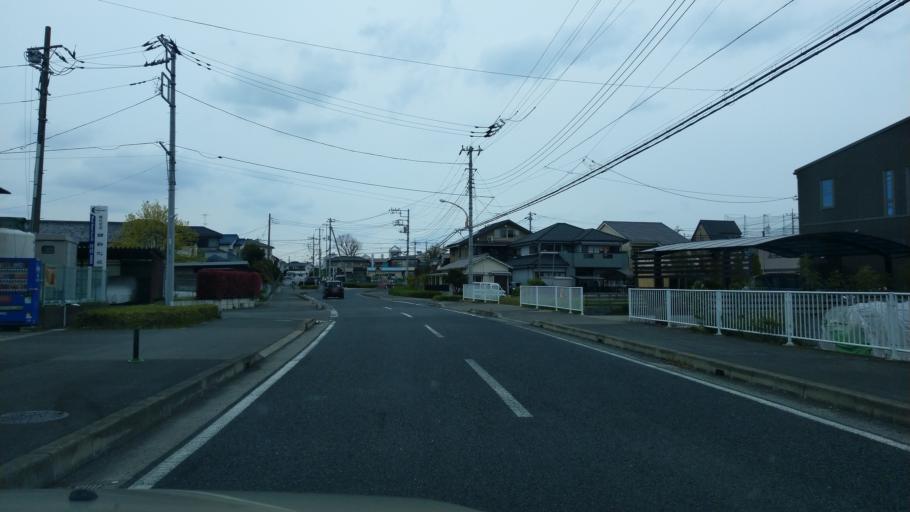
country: JP
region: Saitama
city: Ageoshimo
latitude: 35.9287
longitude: 139.5838
